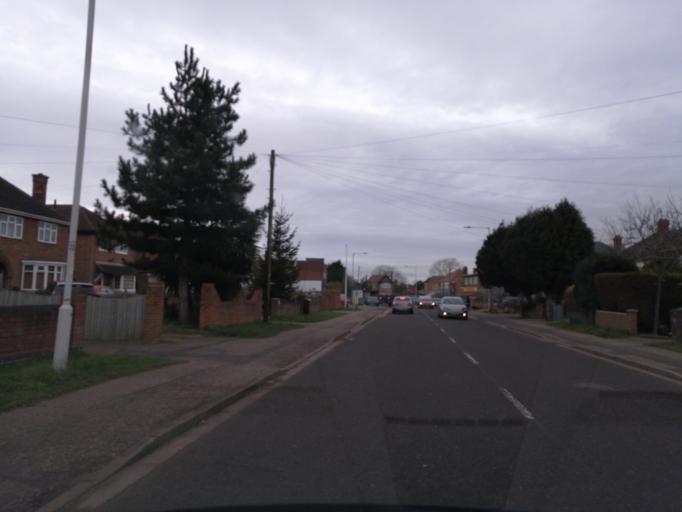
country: GB
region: England
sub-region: Peterborough
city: Peterborough
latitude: 52.5924
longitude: -0.2326
